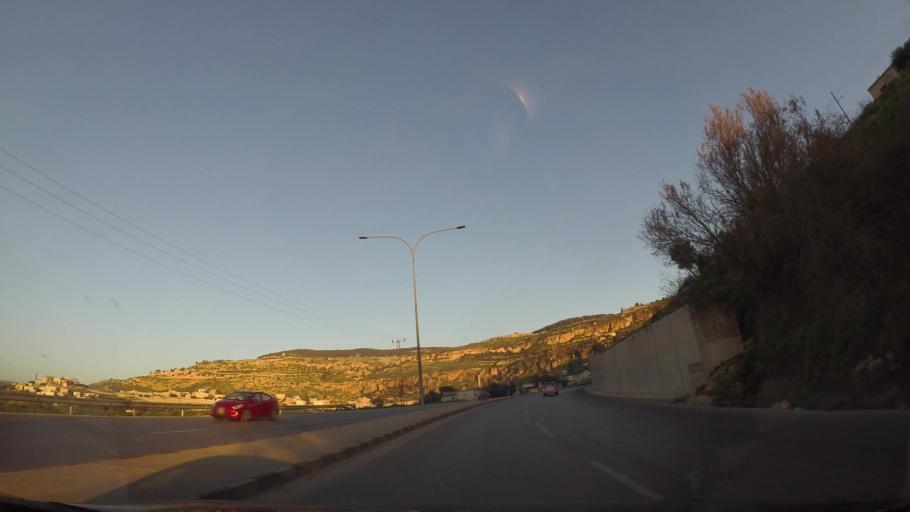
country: JO
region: Amman
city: Umm as Summaq
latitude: 31.8632
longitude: 35.7554
